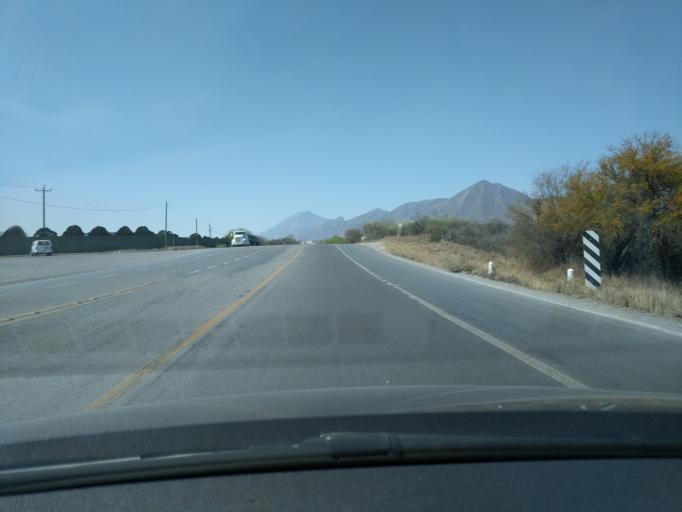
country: MX
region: Nuevo Leon
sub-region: Salinas Victoria
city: Las Torres
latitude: 25.9166
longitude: -100.3653
